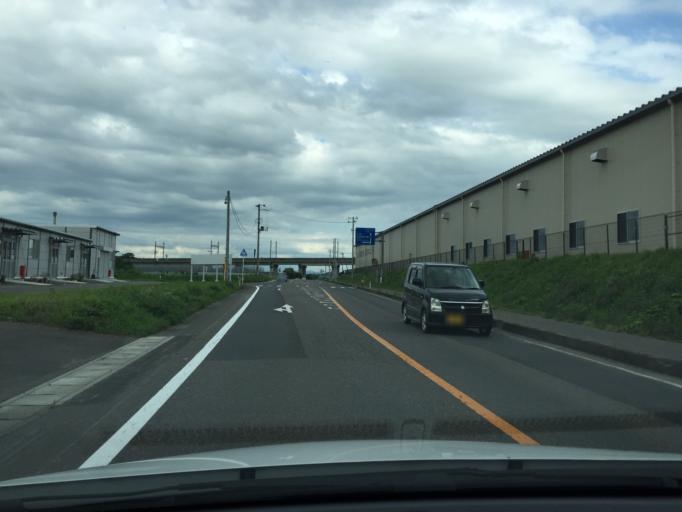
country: JP
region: Fukushima
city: Sukagawa
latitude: 37.2063
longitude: 140.2618
